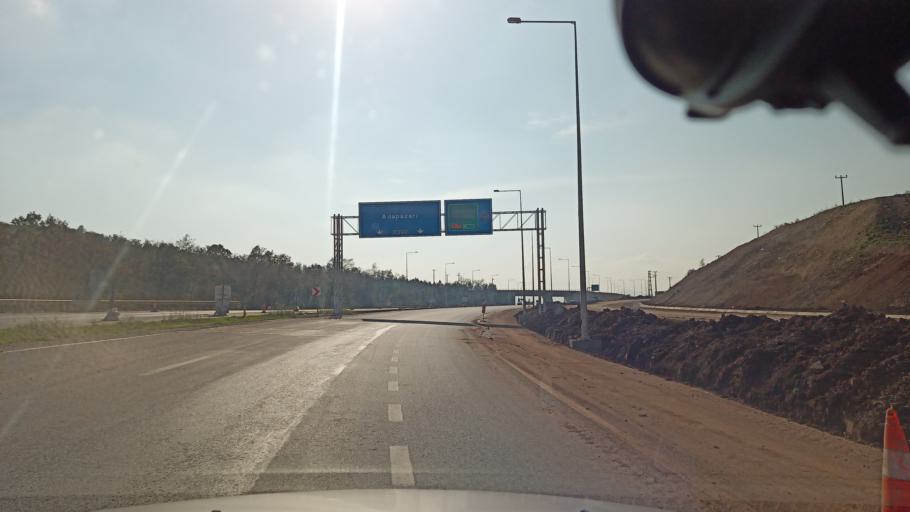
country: TR
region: Sakarya
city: Adapazari
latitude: 40.8556
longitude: 30.3615
